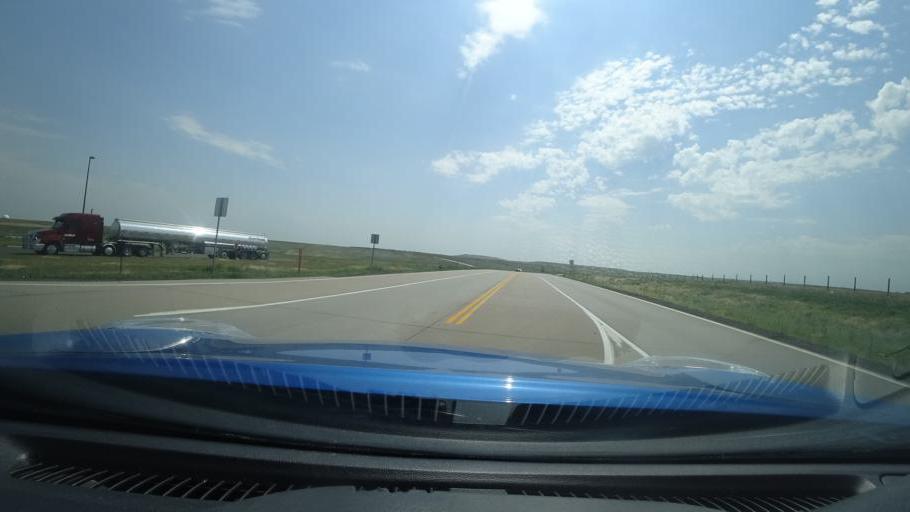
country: US
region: Colorado
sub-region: Adams County
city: Aurora
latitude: 39.6810
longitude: -104.7509
